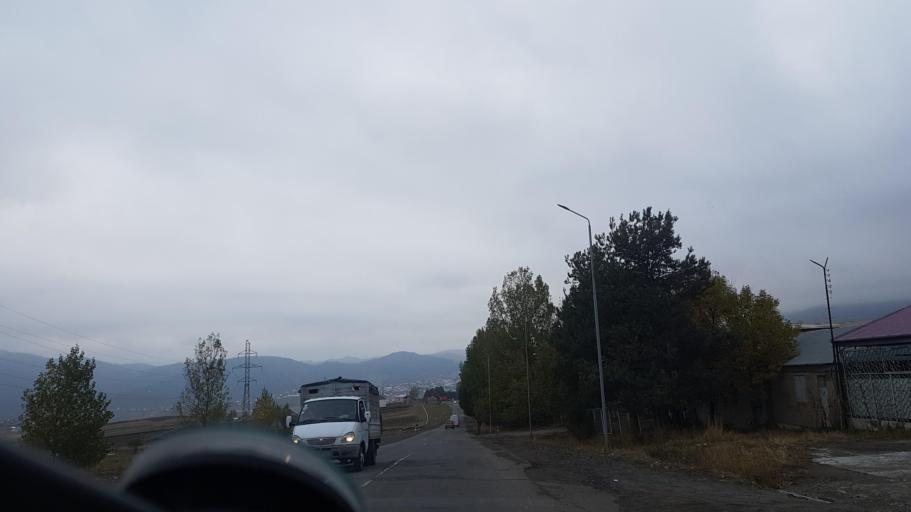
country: AZ
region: Gadabay Rayon
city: Ariqdam
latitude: 40.6118
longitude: 45.8129
